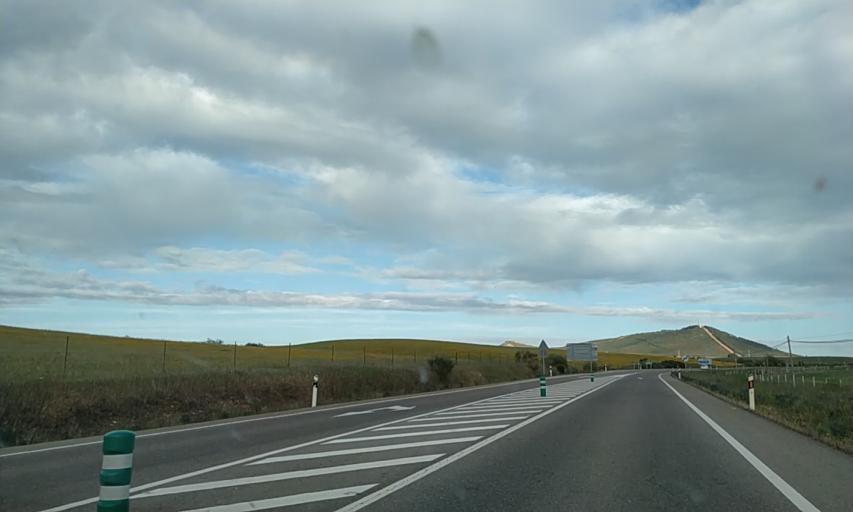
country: ES
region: Extremadura
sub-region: Provincia de Caceres
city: Pedroso de Acim
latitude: 39.8407
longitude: -6.3988
